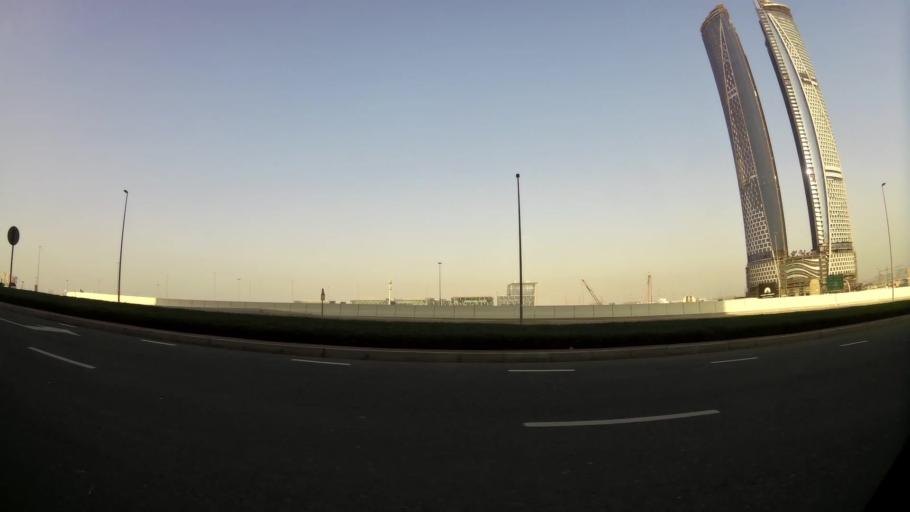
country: AE
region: Dubai
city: Dubai
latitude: 25.1889
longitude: 55.2893
